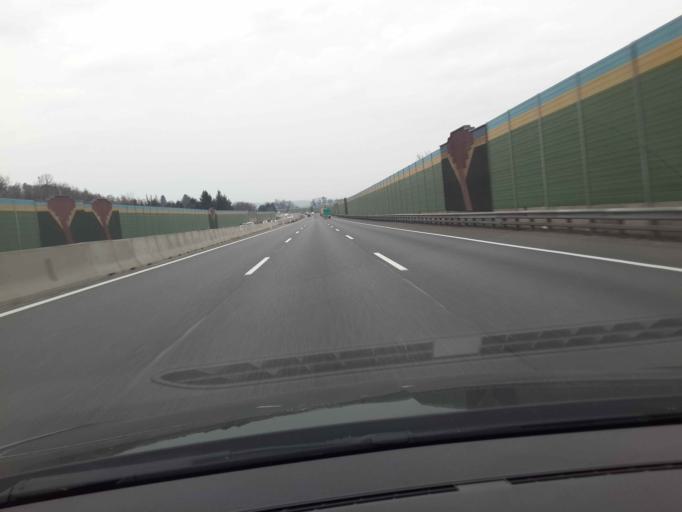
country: AT
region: Lower Austria
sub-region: Politischer Bezirk Sankt Polten
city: Kirchstetten
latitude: 48.1810
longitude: 15.8193
